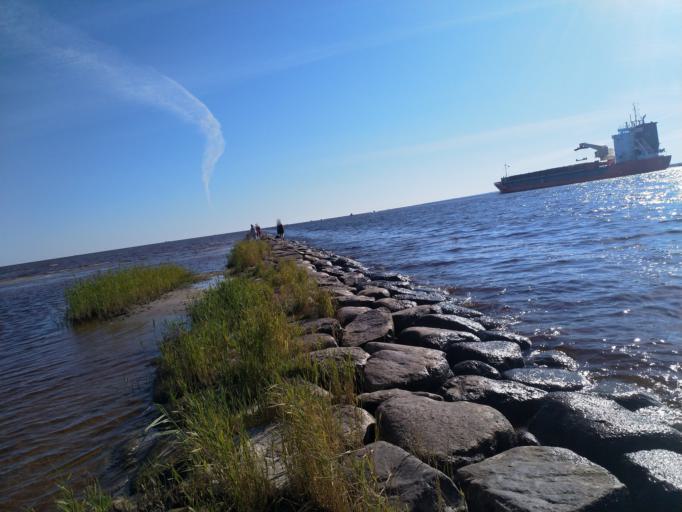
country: EE
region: Paernumaa
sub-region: Paernu linn
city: Parnu
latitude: 58.3774
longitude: 24.4789
